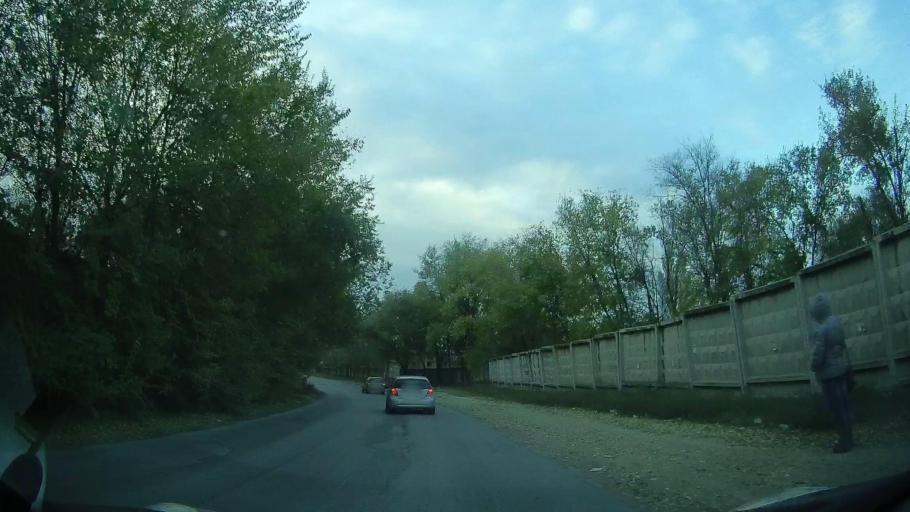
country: RU
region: Rostov
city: Severnyy
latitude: 47.2648
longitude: 39.6458
